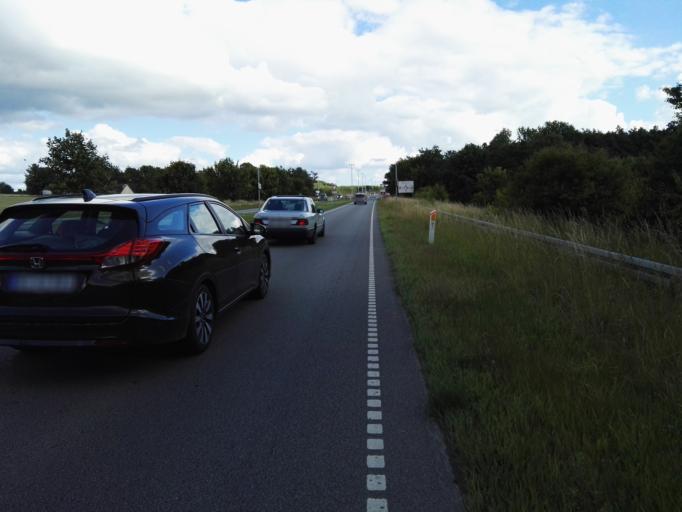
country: DK
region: Capital Region
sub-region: Frederikssund Kommune
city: Frederikssund
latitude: 55.8477
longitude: 12.0922
